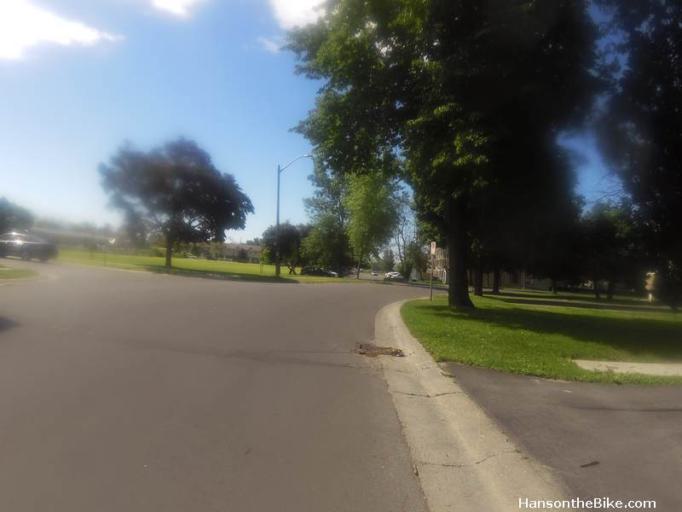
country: CA
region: Ontario
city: Kingston
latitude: 44.2292
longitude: -76.5292
